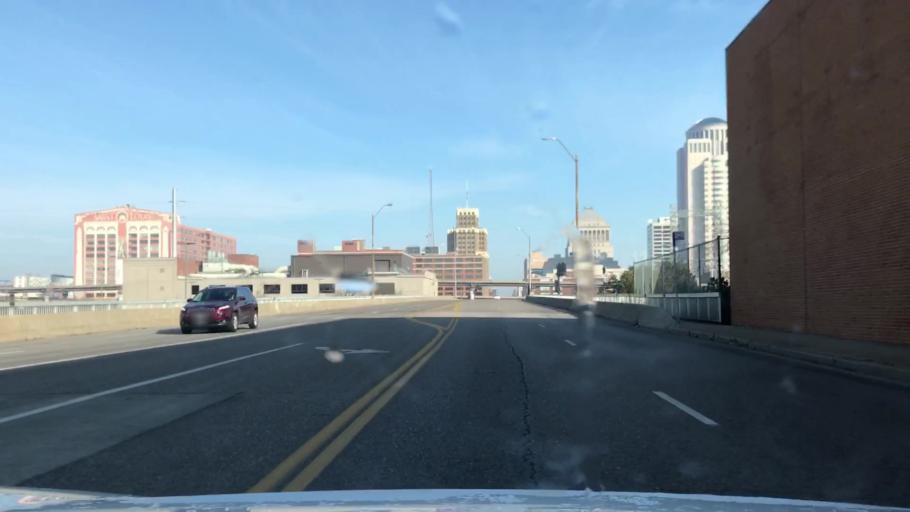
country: US
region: Missouri
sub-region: City of Saint Louis
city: St. Louis
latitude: 38.6192
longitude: -90.2015
